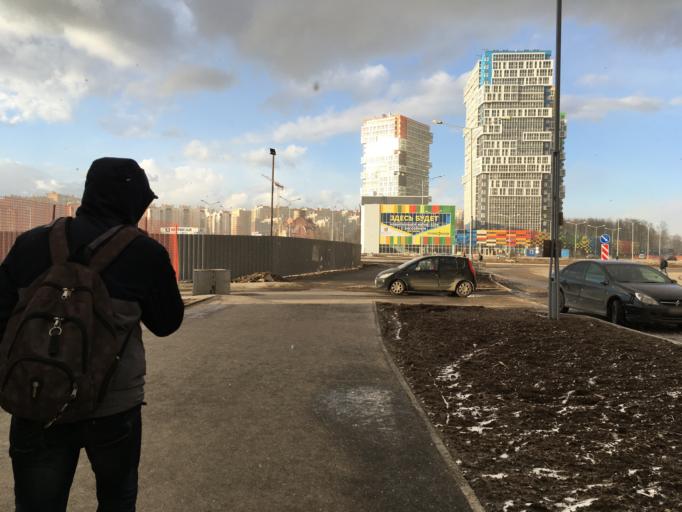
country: RU
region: Leningrad
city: Rybatskoye
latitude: 59.9077
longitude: 30.5127
